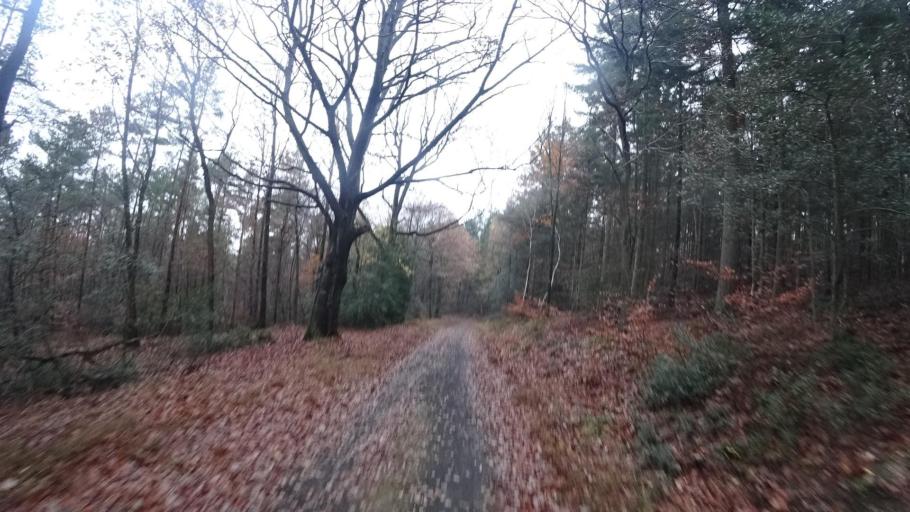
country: DE
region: Rheinland-Pfalz
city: Schalkenbach
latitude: 50.5211
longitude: 7.1308
